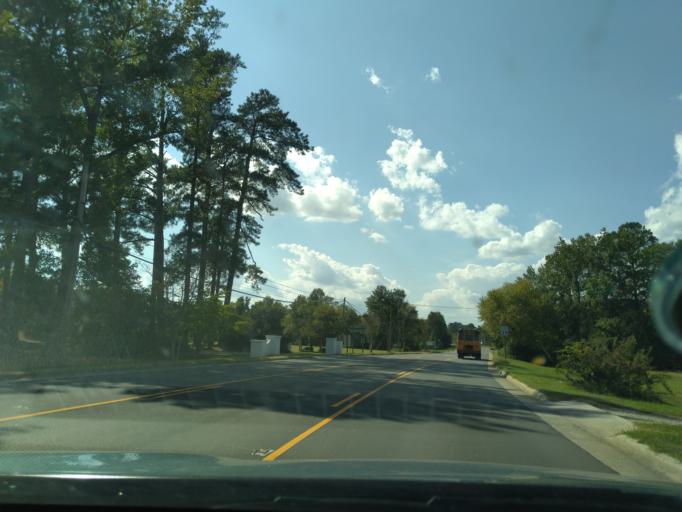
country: US
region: North Carolina
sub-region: Martin County
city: Robersonville
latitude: 35.8241
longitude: -77.2663
